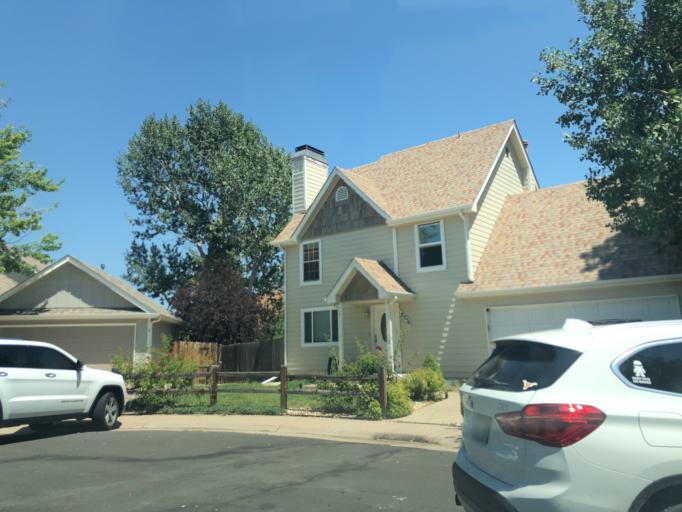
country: US
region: Colorado
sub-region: Arapahoe County
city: Dove Valley
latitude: 39.6246
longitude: -104.7774
